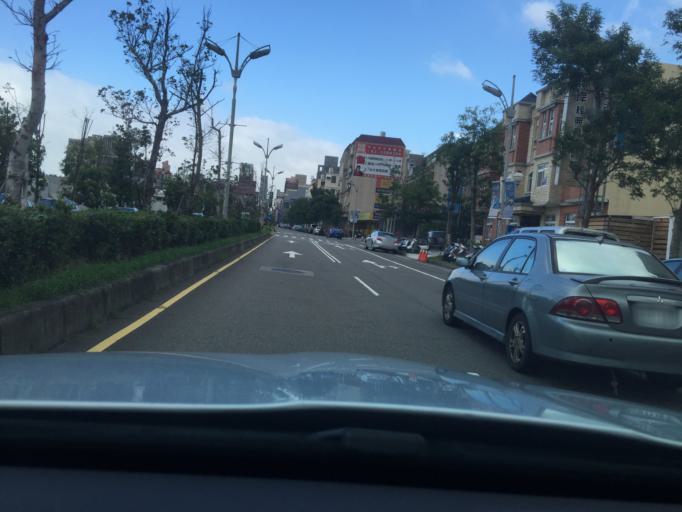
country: TW
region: Taiwan
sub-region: Hsinchu
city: Zhubei
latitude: 24.8221
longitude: 121.0068
